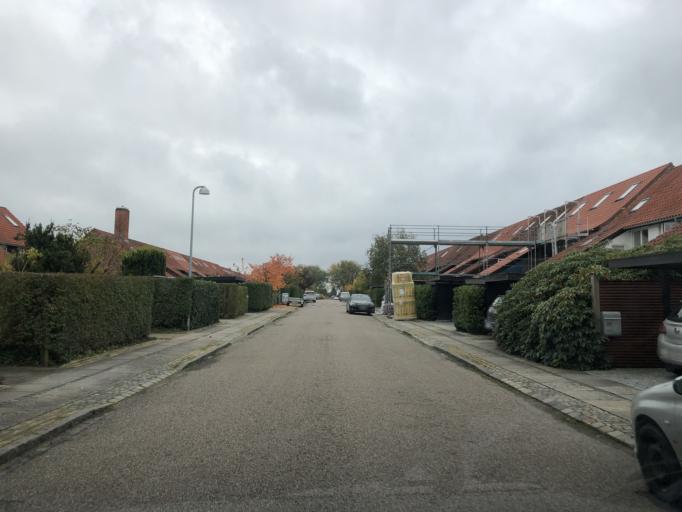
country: DK
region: Capital Region
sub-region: Rudersdal Kommune
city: Holte
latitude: 55.7877
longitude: 12.4685
